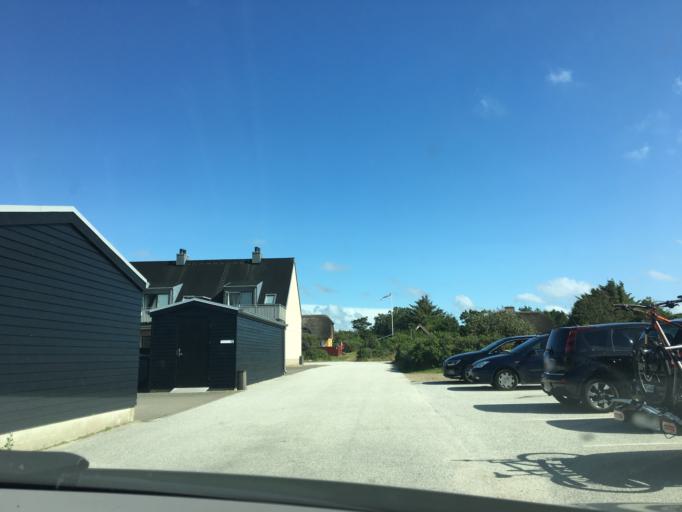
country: DK
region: South Denmark
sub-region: Varde Kommune
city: Oksbol
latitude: 55.7387
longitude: 8.1808
